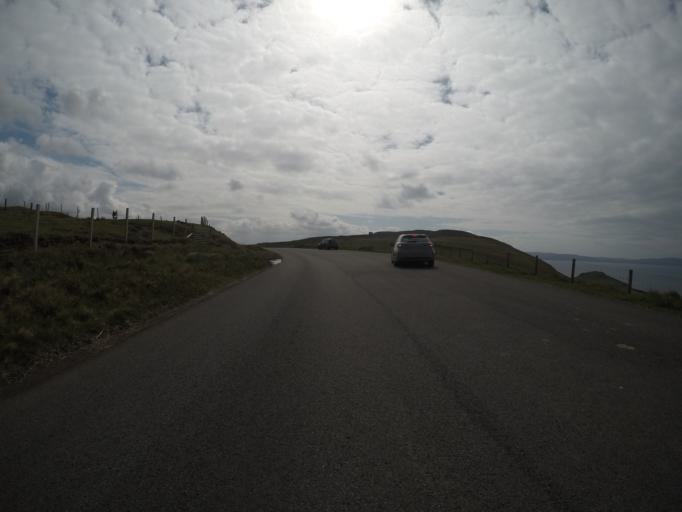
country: GB
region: Scotland
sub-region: Highland
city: Portree
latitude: 57.6023
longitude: -6.3778
